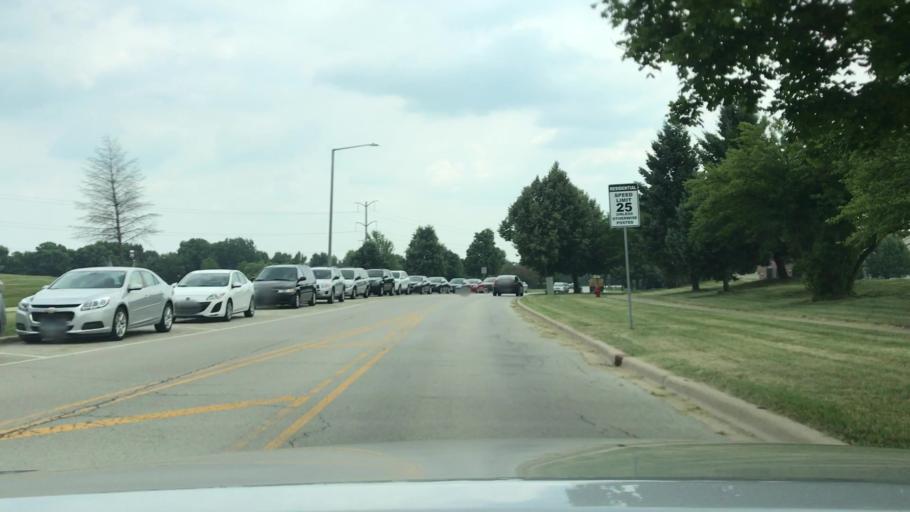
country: US
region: Illinois
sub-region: Will County
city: Plainfield
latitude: 41.6069
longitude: -88.2152
